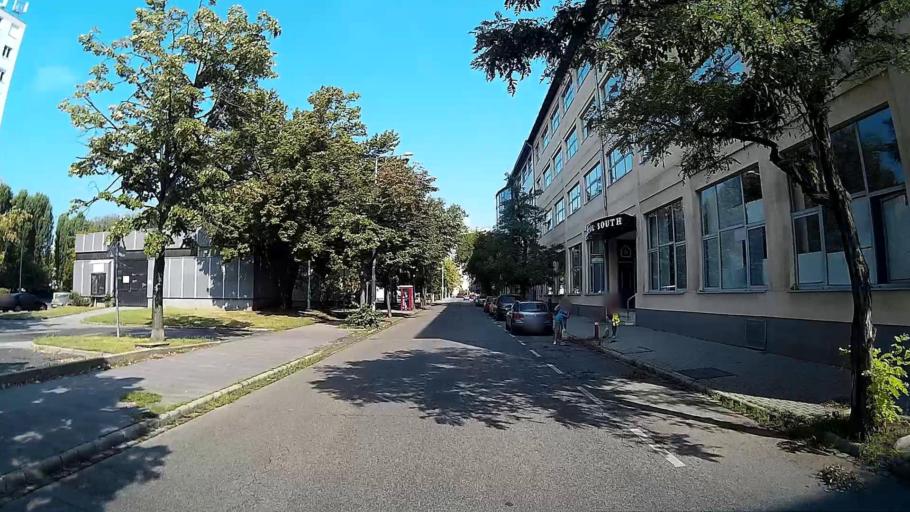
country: HU
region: Budapest
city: Budapest XIII. keruelet
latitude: 47.5253
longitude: 19.0732
